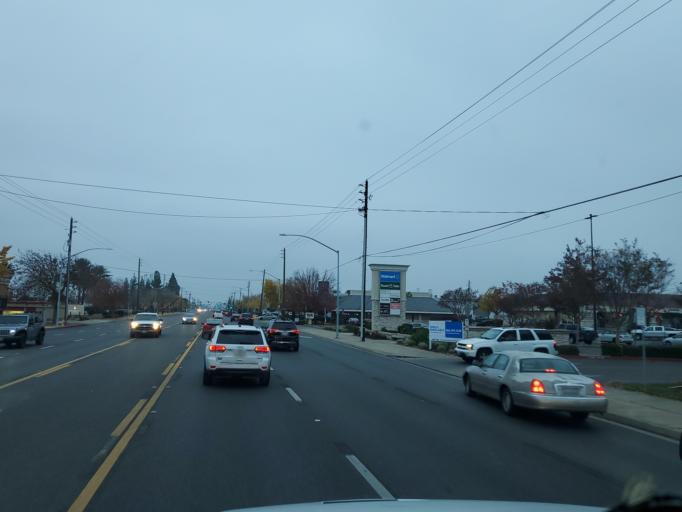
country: US
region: California
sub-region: Stanislaus County
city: Del Rio
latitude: 37.6944
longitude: -120.9943
